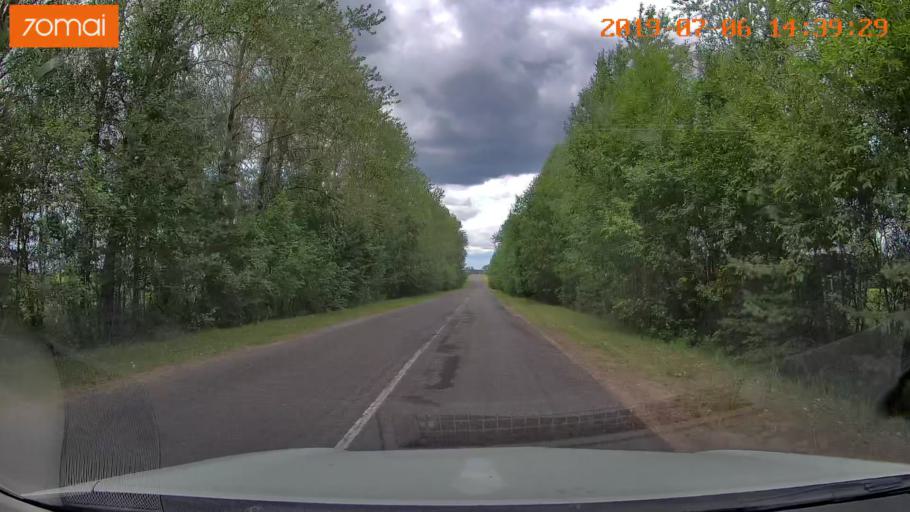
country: BY
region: Minsk
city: Ivyanyets
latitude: 53.9168
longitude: 26.6884
